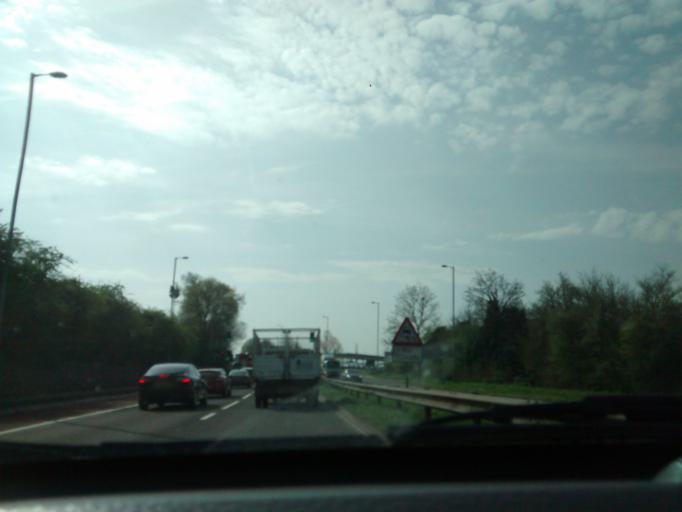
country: GB
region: England
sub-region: Oxfordshire
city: Yarnton
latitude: 51.7908
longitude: -1.2829
